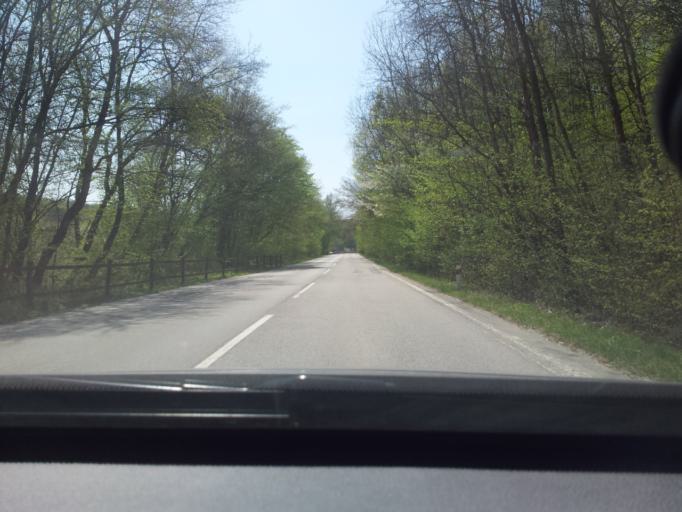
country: SK
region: Nitriansky
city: Zlate Moravce
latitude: 48.4553
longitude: 18.4109
